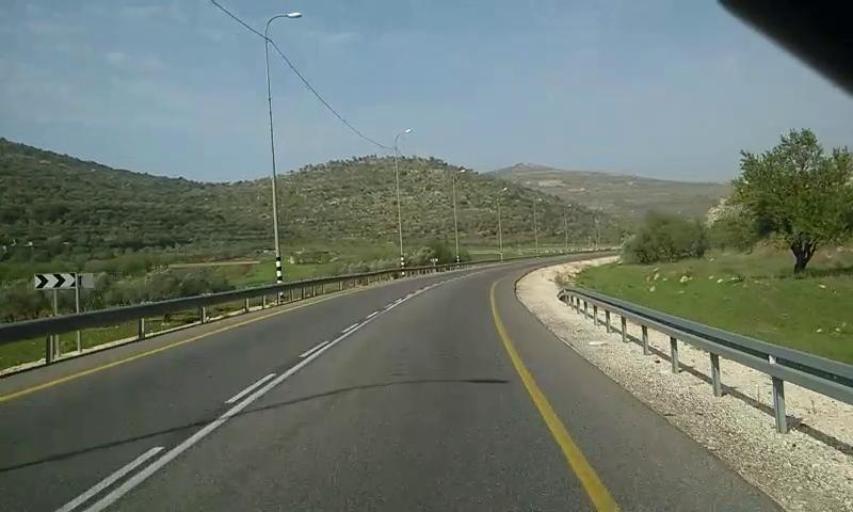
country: PS
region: West Bank
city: Al Lubban ash Sharqiyah
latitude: 32.0663
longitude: 35.2469
